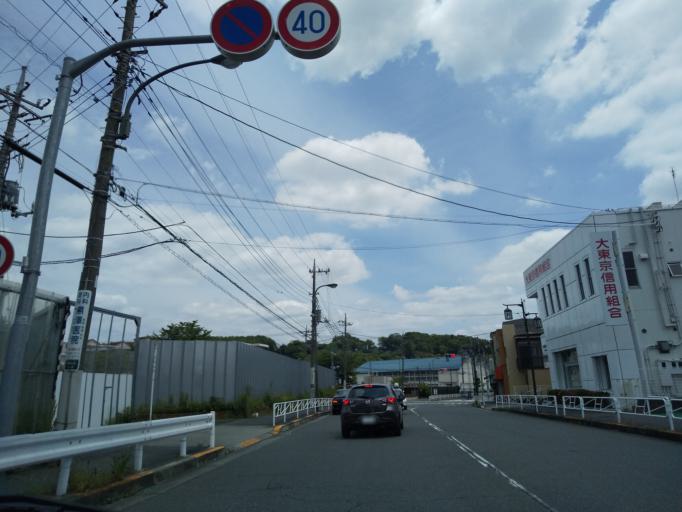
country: JP
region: Tokyo
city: Hachioji
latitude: 35.6732
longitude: 139.3255
